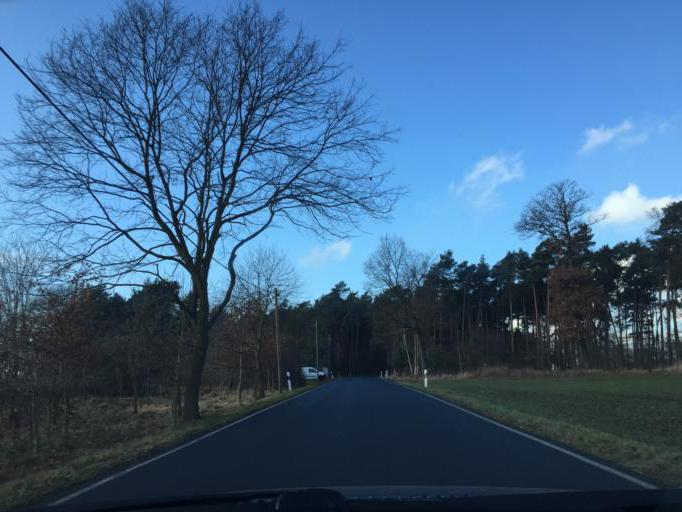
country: DE
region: Saxony
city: Thiendorf
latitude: 51.2815
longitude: 13.7385
